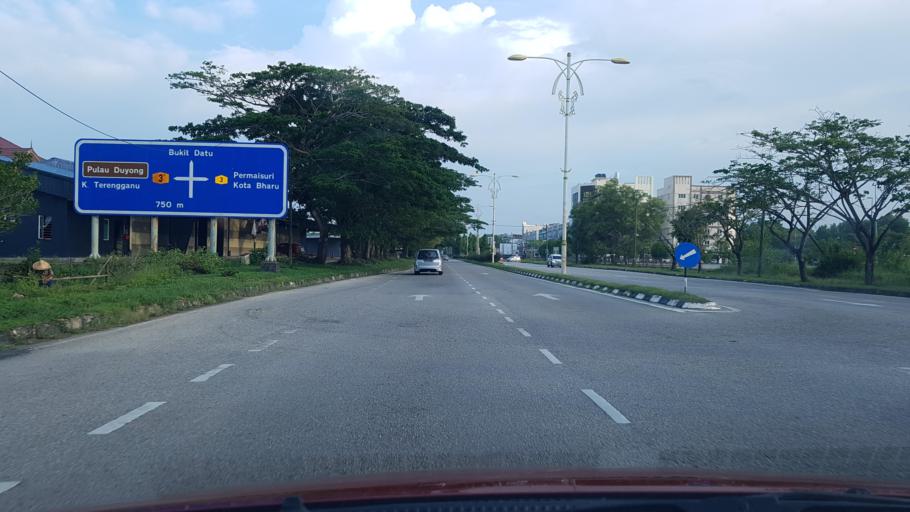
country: MY
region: Terengganu
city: Kuala Terengganu
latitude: 5.3511
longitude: 103.1031
